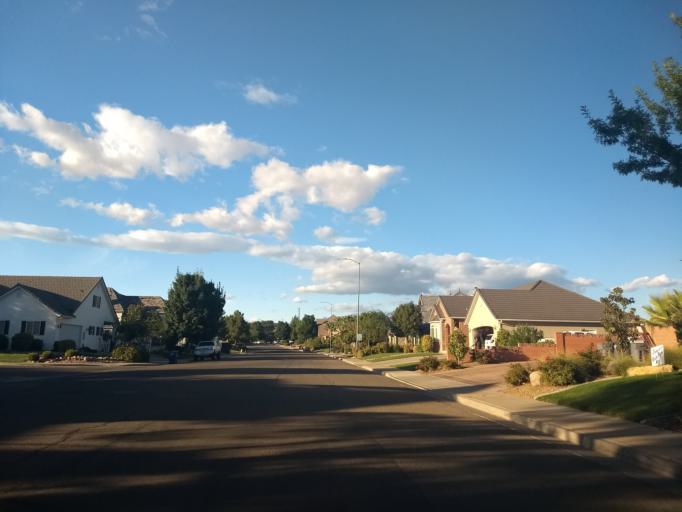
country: US
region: Utah
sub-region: Washington County
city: Saint George
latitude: 37.0901
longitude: -113.5640
